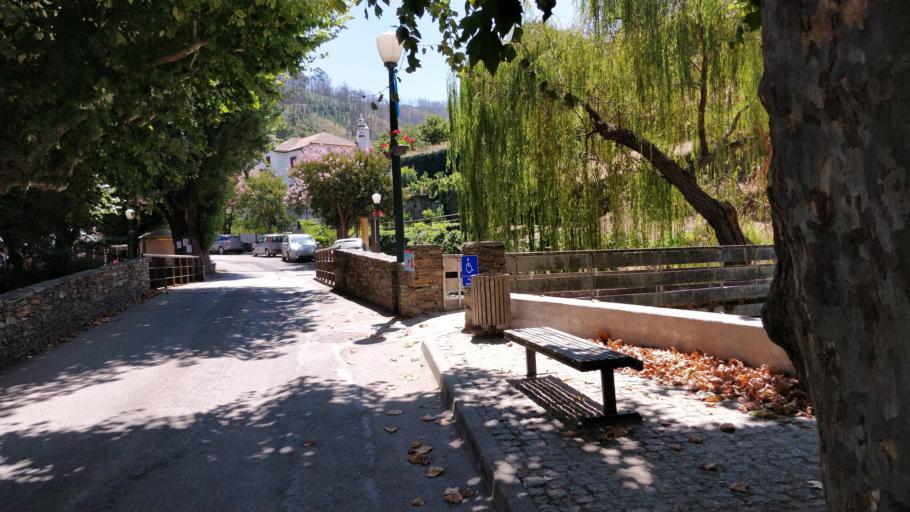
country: PT
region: Coimbra
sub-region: Arganil
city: Arganil
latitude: 40.2289
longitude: -7.9451
